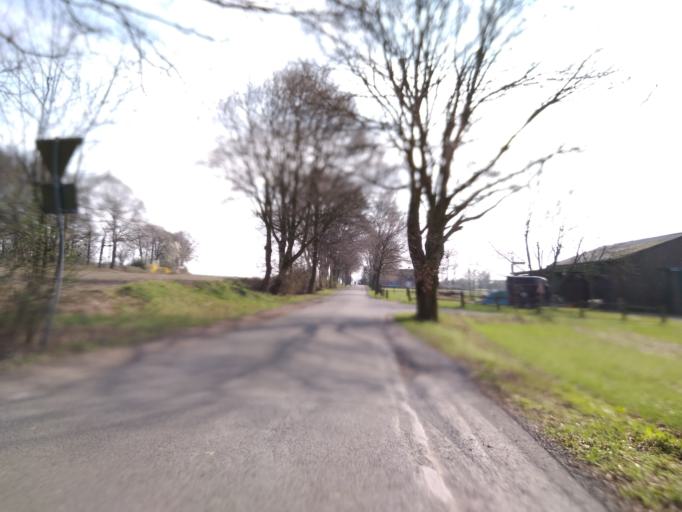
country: DE
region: North Rhine-Westphalia
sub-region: Regierungsbezirk Munster
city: Gladbeck
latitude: 51.5997
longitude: 6.9459
